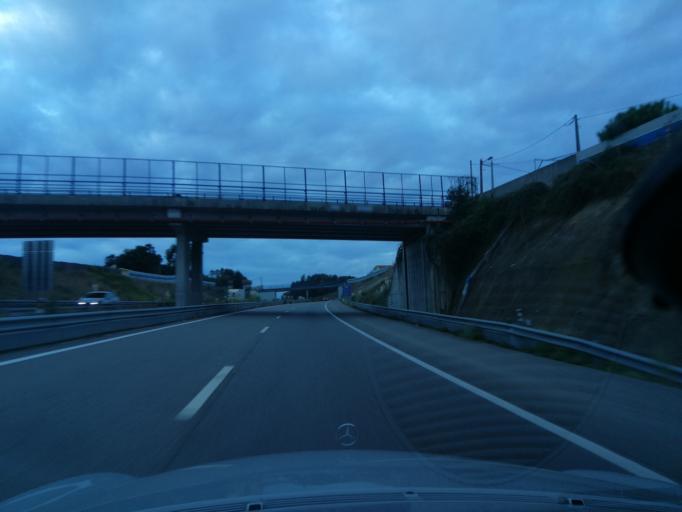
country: PT
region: Aveiro
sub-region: Estarreja
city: Beduido
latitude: 40.7663
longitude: -8.5532
